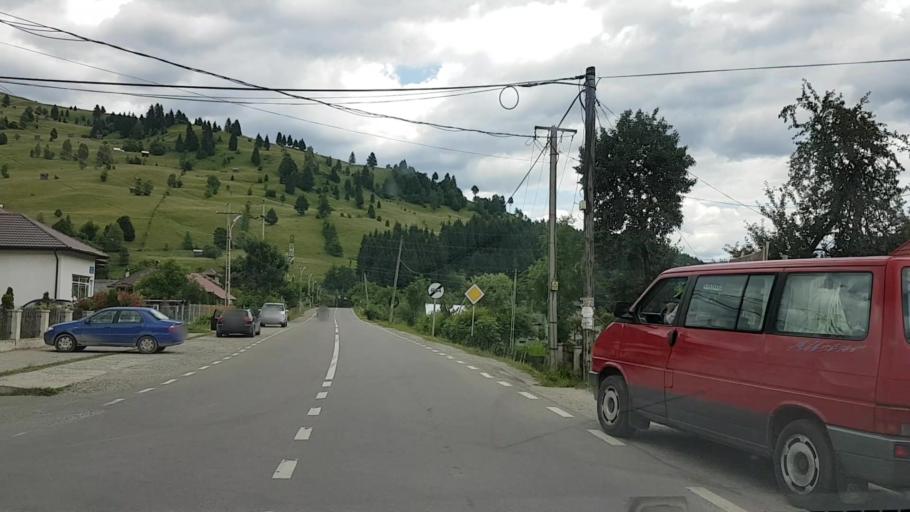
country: RO
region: Neamt
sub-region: Comuna Borca
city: Borca
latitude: 47.1788
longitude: 25.7869
